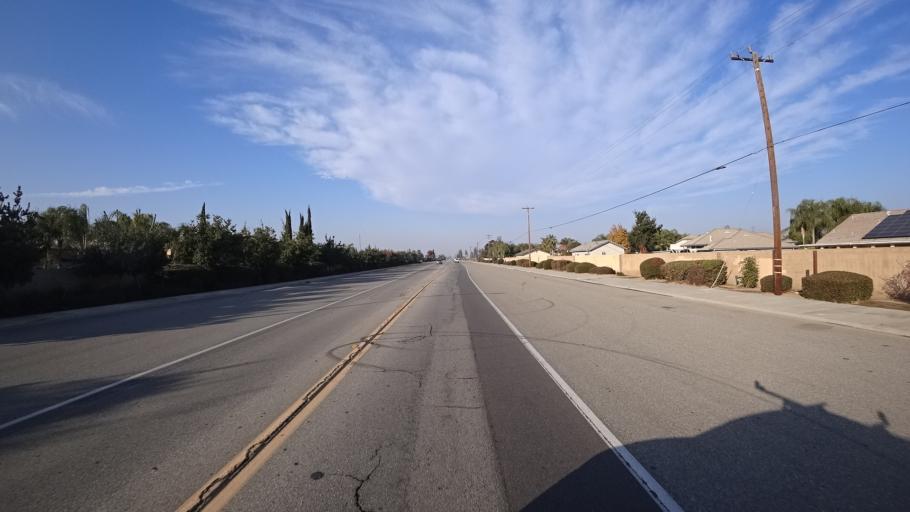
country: US
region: California
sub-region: Kern County
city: Rosedale
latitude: 35.3835
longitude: -119.1695
